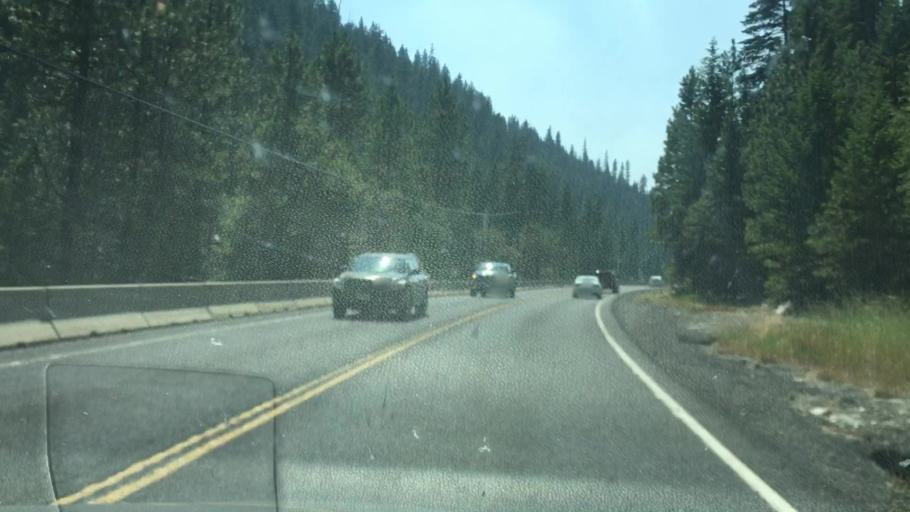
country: US
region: Idaho
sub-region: Valley County
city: McCall
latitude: 45.1297
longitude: -116.2859
